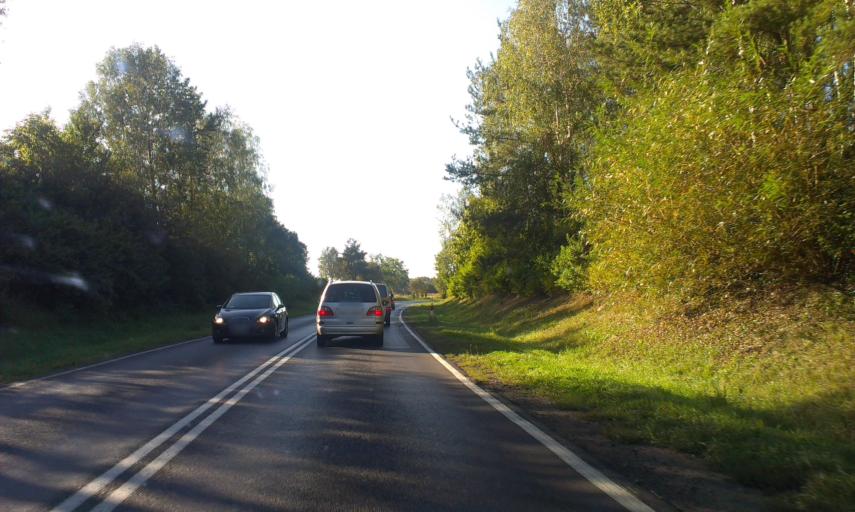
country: PL
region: Kujawsko-Pomorskie
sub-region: Powiat swiecki
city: Swiecie
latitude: 53.4140
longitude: 18.3652
